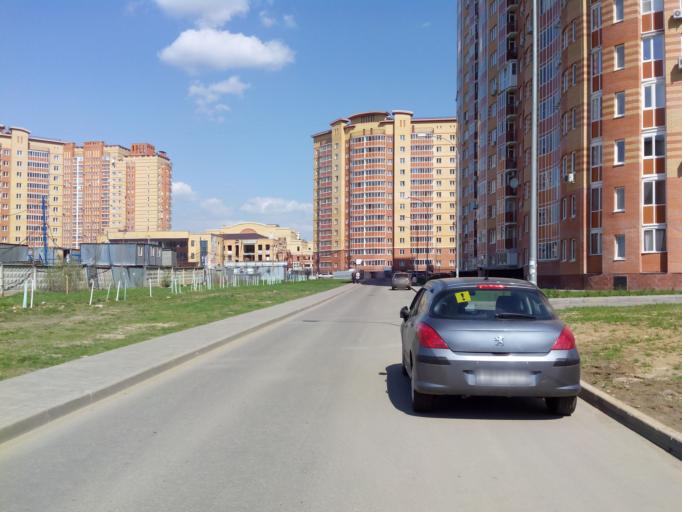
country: RU
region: Moskovskaya
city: Lesnoy Gorodok
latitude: 55.6581
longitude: 37.2282
